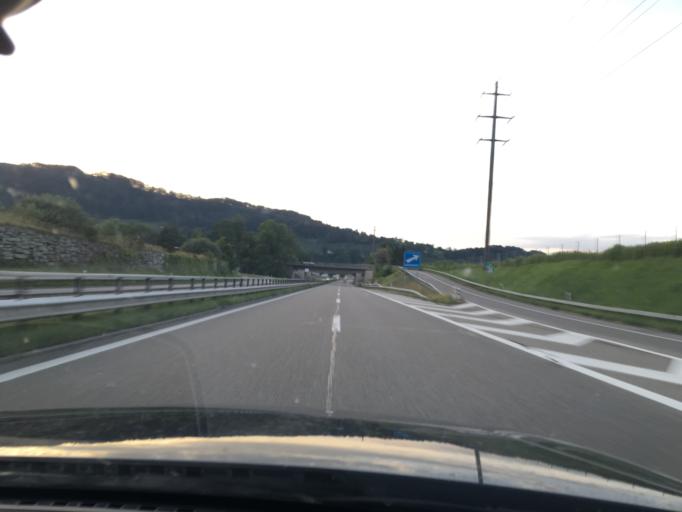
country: CH
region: Saint Gallen
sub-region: Wahlkreis Rheintal
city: Au
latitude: 47.4283
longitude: 9.6451
